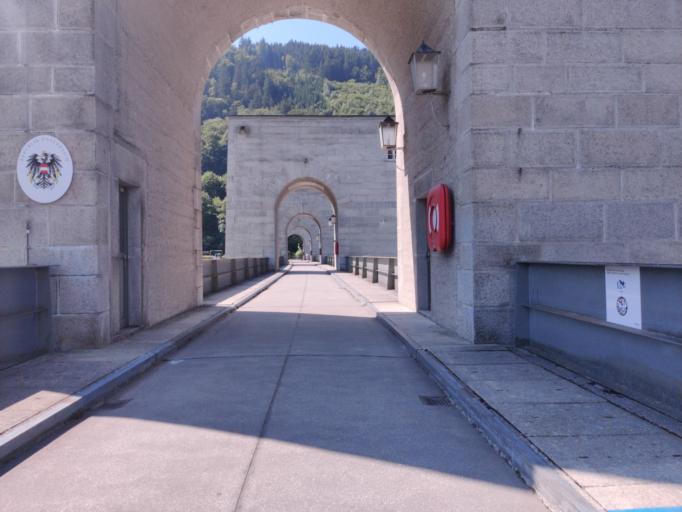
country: DE
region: Bavaria
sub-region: Lower Bavaria
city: Untergriesbach
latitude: 48.5173
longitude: 13.7069
